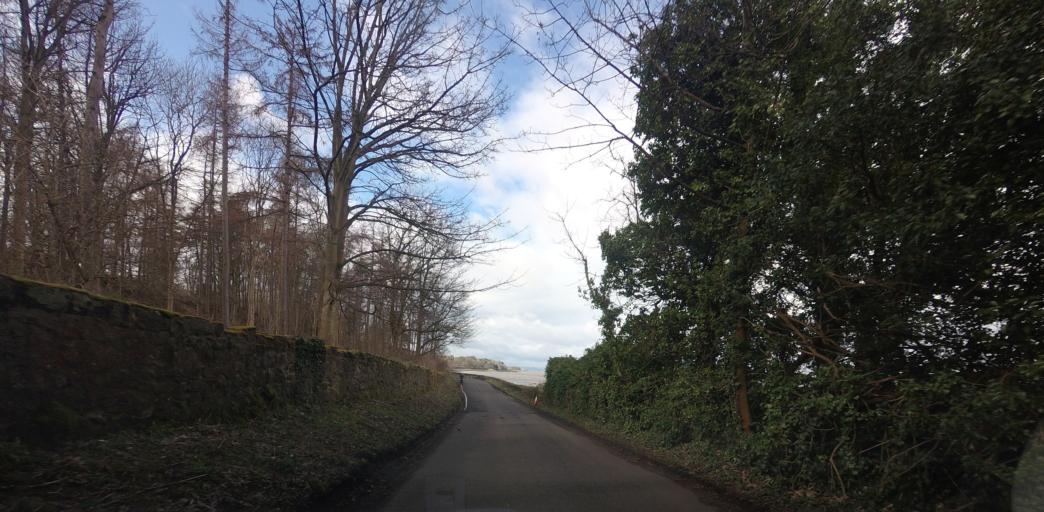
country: GB
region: Scotland
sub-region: Edinburgh
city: Queensferry
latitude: 55.9937
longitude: -3.4245
